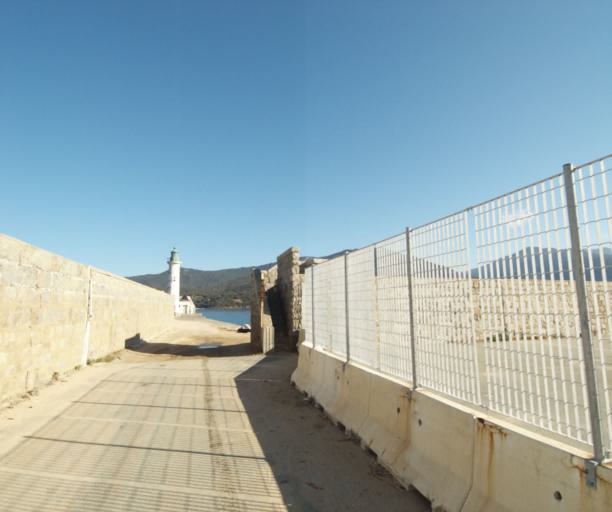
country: FR
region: Corsica
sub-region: Departement de la Corse-du-Sud
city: Propriano
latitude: 41.6777
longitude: 8.8976
